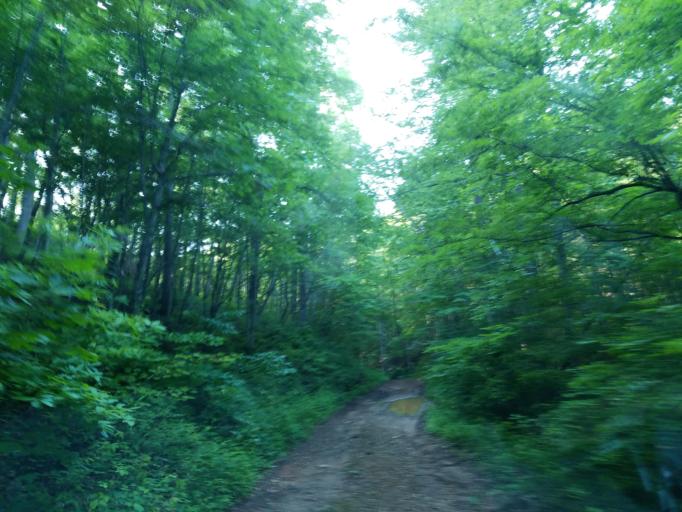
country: US
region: Georgia
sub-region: Fannin County
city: Blue Ridge
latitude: 34.8066
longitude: -84.1703
